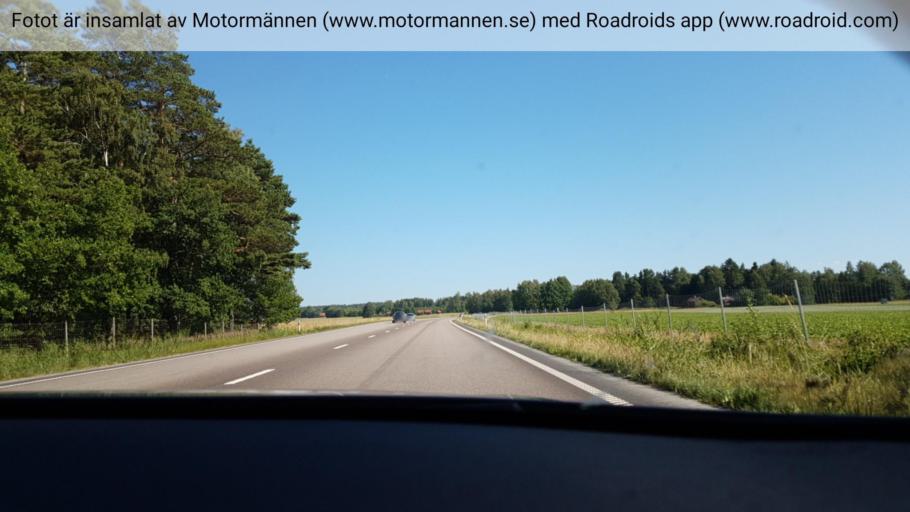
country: SE
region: Vaestra Goetaland
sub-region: Lidkopings Kommun
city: Vinninga
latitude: 58.4568
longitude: 13.2339
